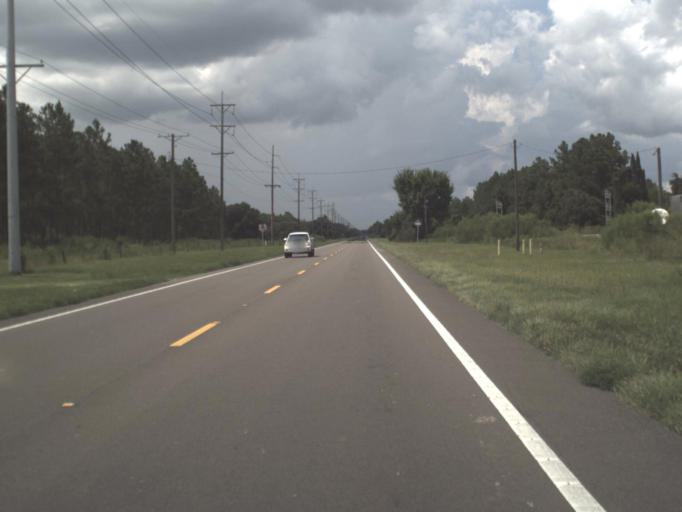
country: US
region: Florida
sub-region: Pasco County
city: Crystal Springs
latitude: 28.1565
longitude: -82.1531
